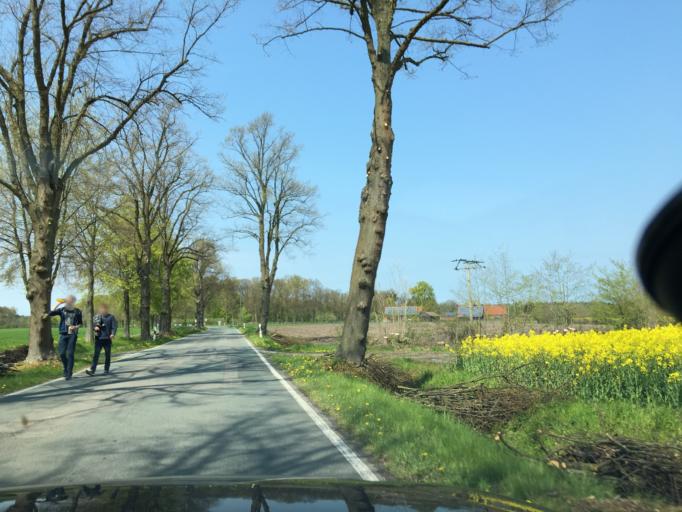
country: DE
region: North Rhine-Westphalia
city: Ludinghausen
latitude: 51.7848
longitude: 7.4348
